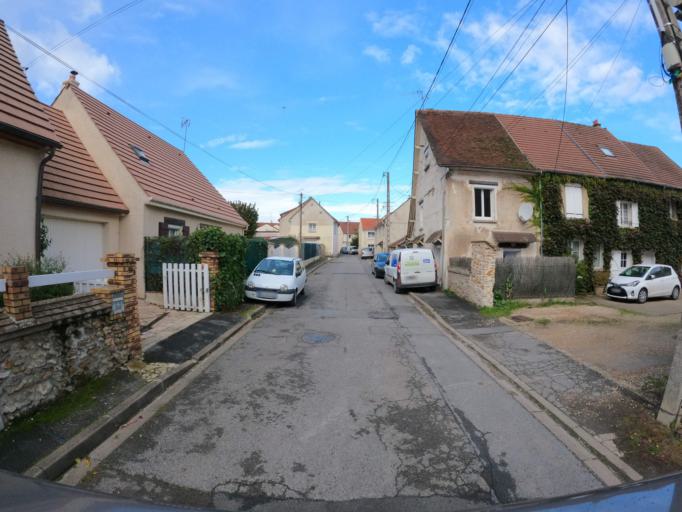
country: FR
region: Ile-de-France
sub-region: Departement de Seine-et-Marne
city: Saint-Germain-sur-Morin
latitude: 48.8808
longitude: 2.8545
